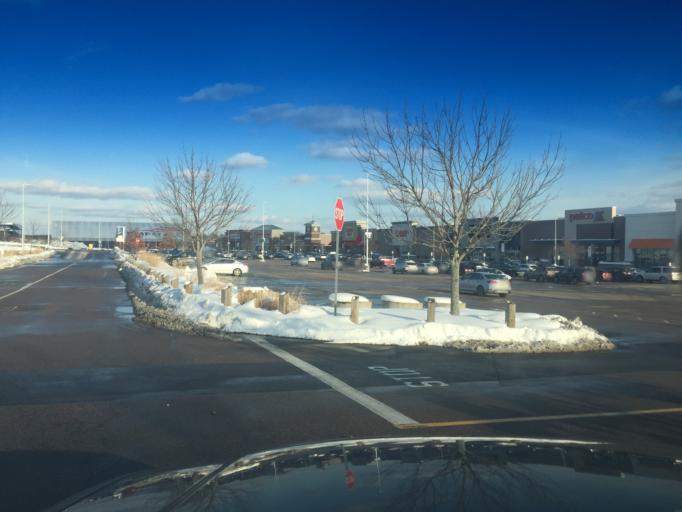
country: US
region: Massachusetts
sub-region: Norfolk County
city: Foxborough
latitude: 42.0869
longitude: -71.2720
